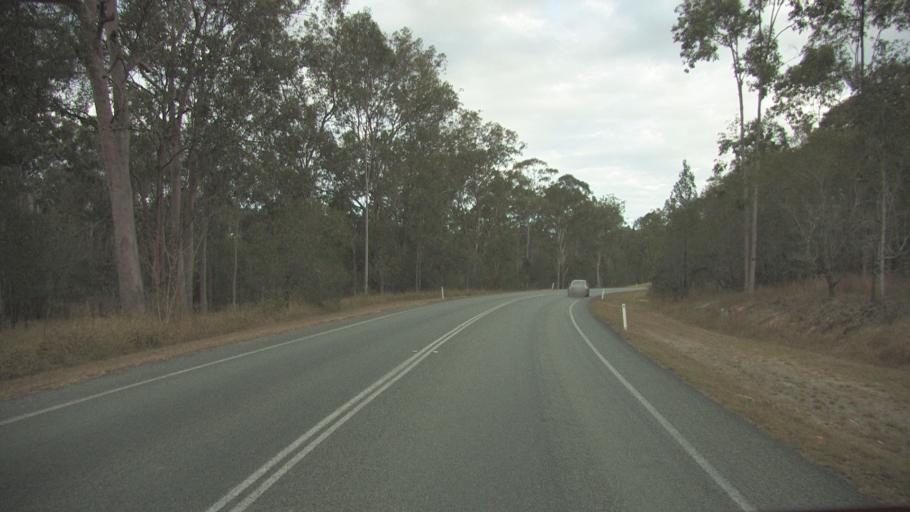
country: AU
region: Queensland
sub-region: Logan
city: Cedar Vale
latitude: -27.9016
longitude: 153.0906
